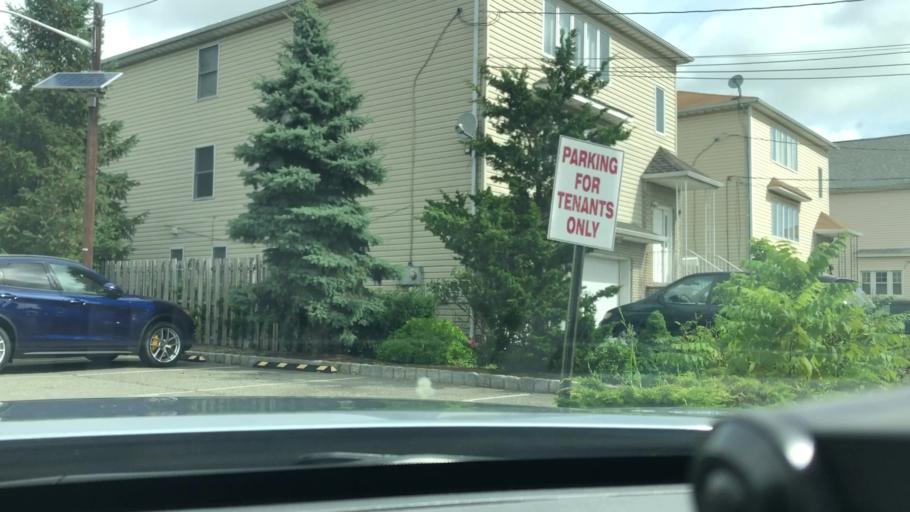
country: US
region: New Jersey
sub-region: Union County
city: Linden
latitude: 40.6333
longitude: -74.2573
